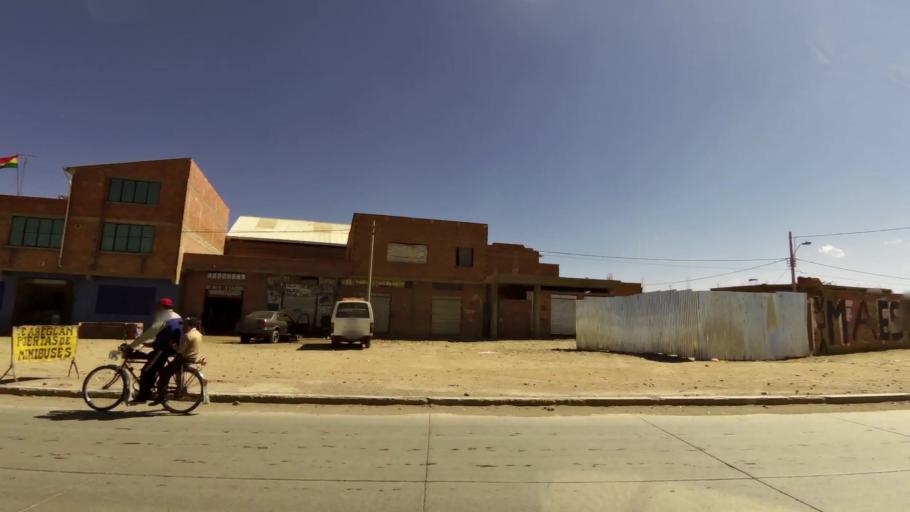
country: BO
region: La Paz
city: La Paz
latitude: -16.5109
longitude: -68.2147
